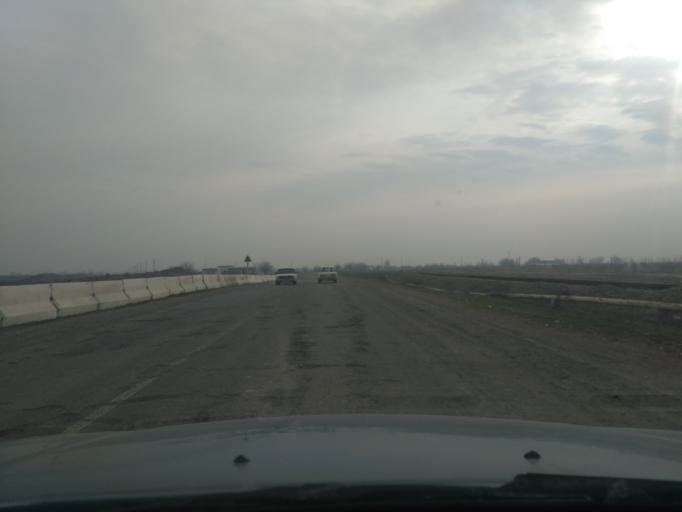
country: UZ
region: Sirdaryo
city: Sirdaryo
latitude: 40.8255
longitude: 68.6230
